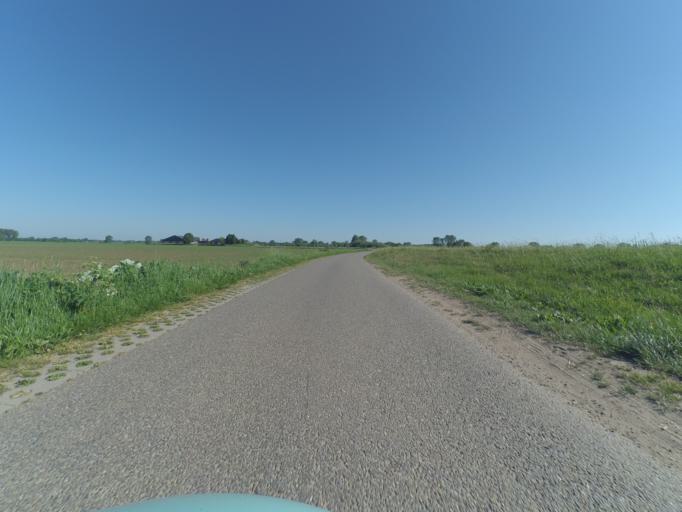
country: NL
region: Gelderland
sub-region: Gemeente Lochem
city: Gorssel
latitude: 52.2108
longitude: 6.1805
